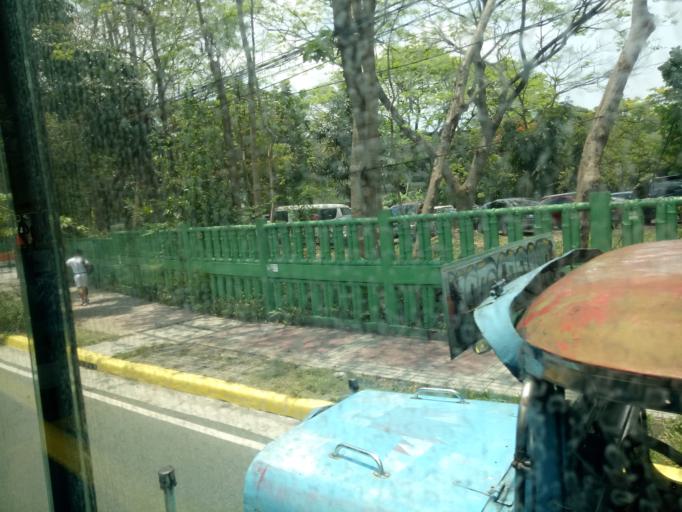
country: PH
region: Metro Manila
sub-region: Quezon City
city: Quezon City
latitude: 14.6483
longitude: 121.0484
